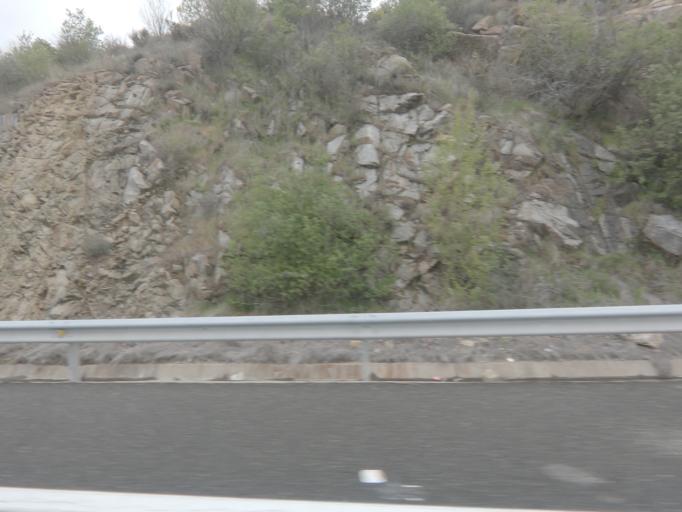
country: ES
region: Extremadura
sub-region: Provincia de Caceres
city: Banos de Montemayor
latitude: 40.3227
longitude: -5.8646
